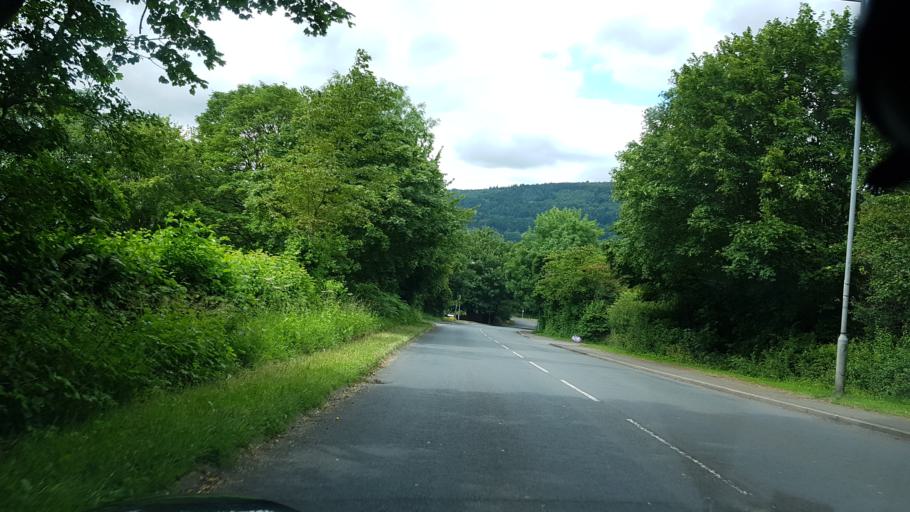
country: GB
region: Wales
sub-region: Monmouthshire
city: Gilwern
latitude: 51.8258
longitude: -3.0818
